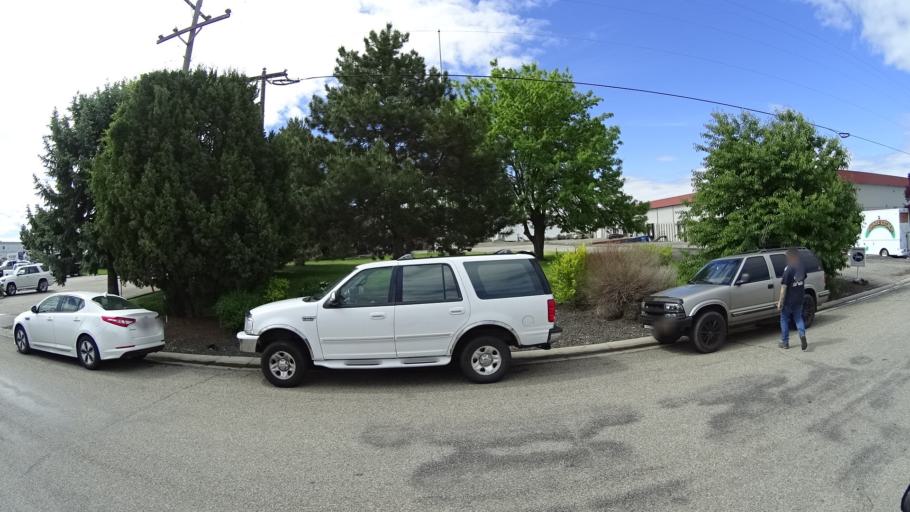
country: US
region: Idaho
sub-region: Ada County
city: Boise
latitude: 43.5628
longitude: -116.1931
